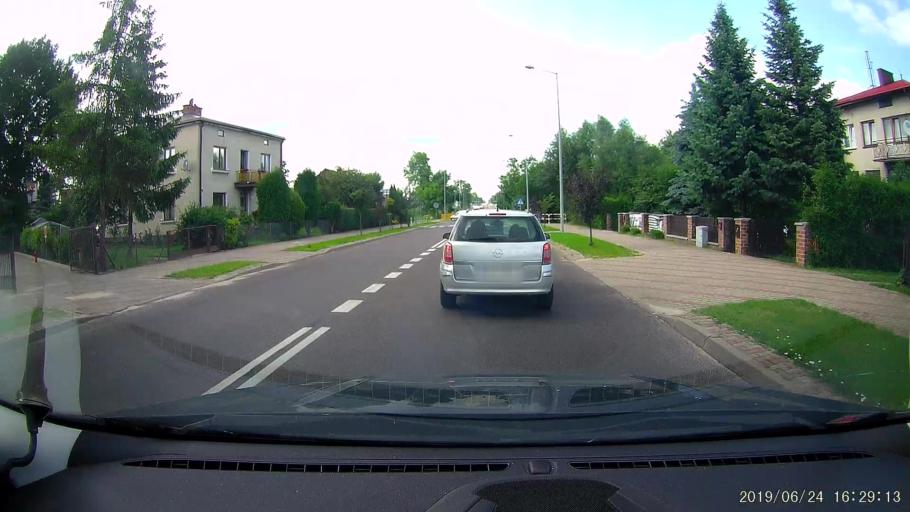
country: PL
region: Lublin Voivodeship
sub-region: Powiat tomaszowski
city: Tomaszow Lubelski
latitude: 50.4578
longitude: 23.4212
